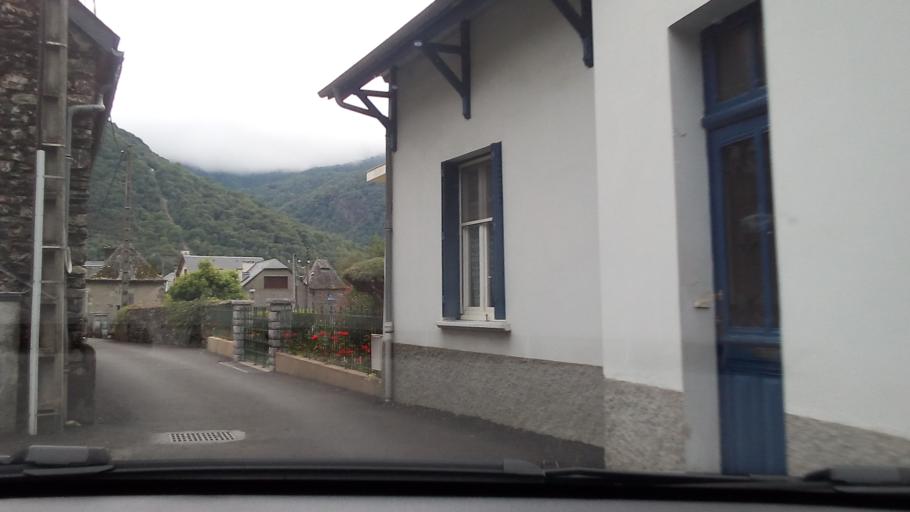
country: FR
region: Midi-Pyrenees
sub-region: Departement des Hautes-Pyrenees
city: Pierrefitte-Nestalas
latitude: 42.9545
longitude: -0.0567
